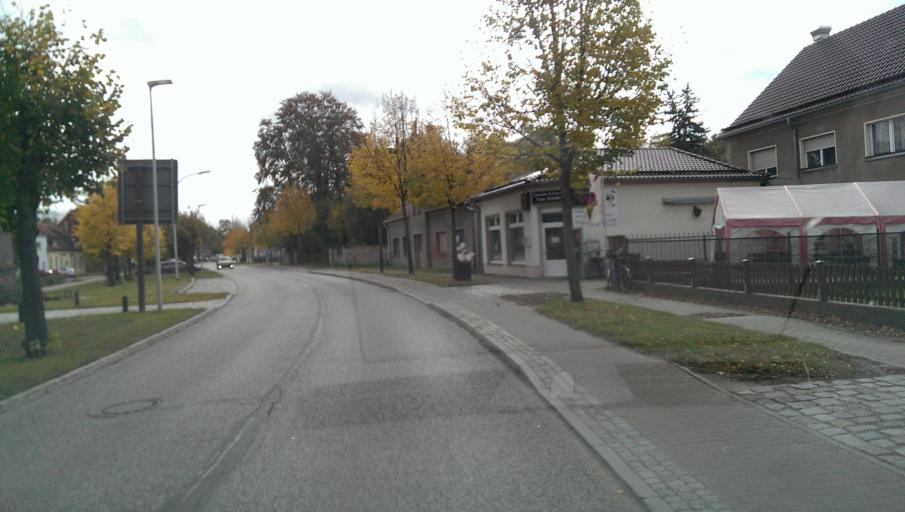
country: DE
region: Brandenburg
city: Doberlug-Kirchhain
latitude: 51.6304
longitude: 13.5623
